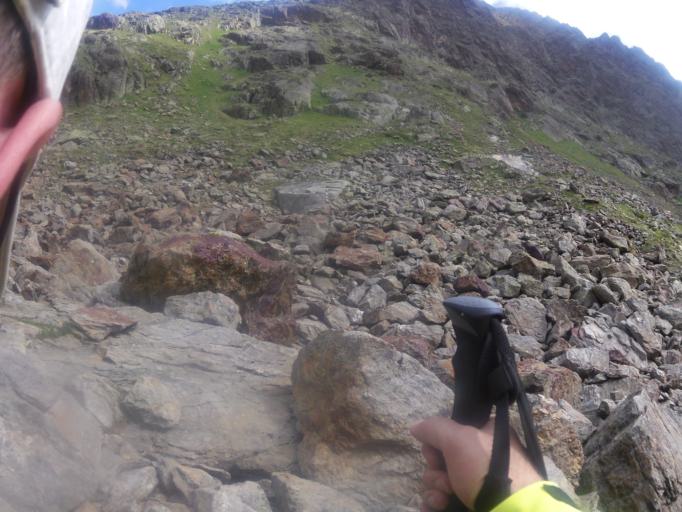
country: IT
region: Trentino-Alto Adige
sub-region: Bolzano
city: Racines
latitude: 46.9926
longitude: 11.2386
